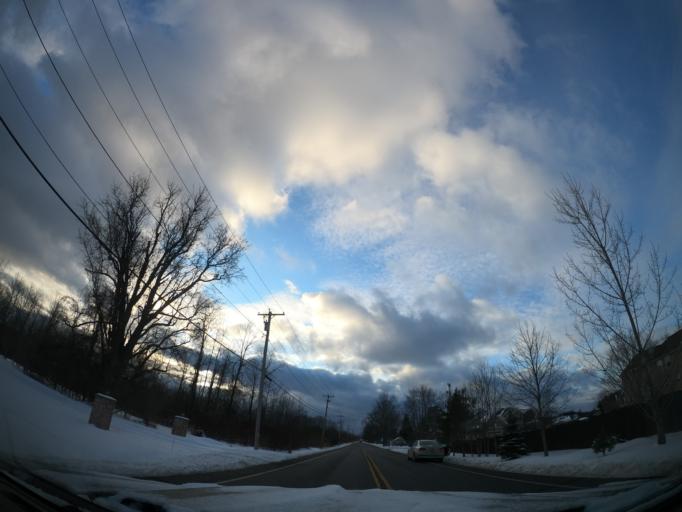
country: US
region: New York
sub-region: Onondaga County
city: Brewerton
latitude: 43.2178
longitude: -76.1142
